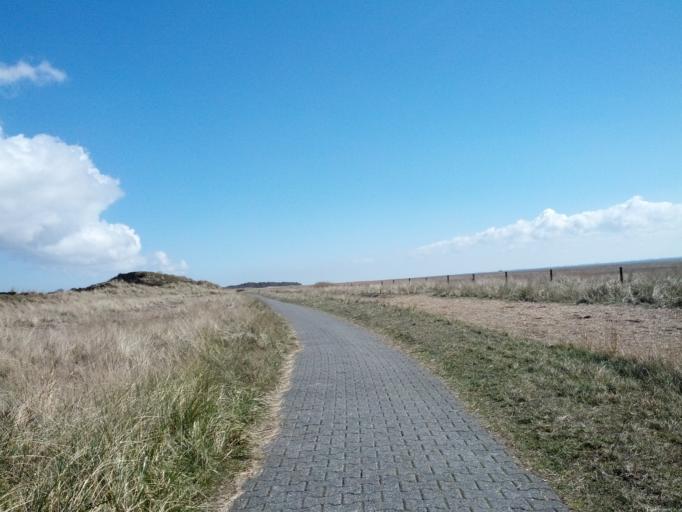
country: DE
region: Lower Saxony
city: Spiekeroog
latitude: 53.7476
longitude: 7.6035
